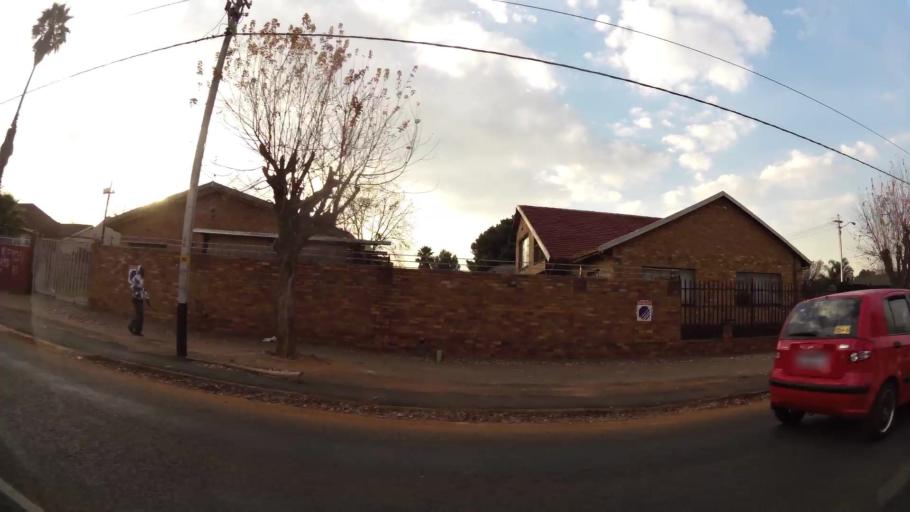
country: ZA
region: Gauteng
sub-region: Ekurhuleni Metropolitan Municipality
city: Germiston
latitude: -26.1822
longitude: 28.1722
